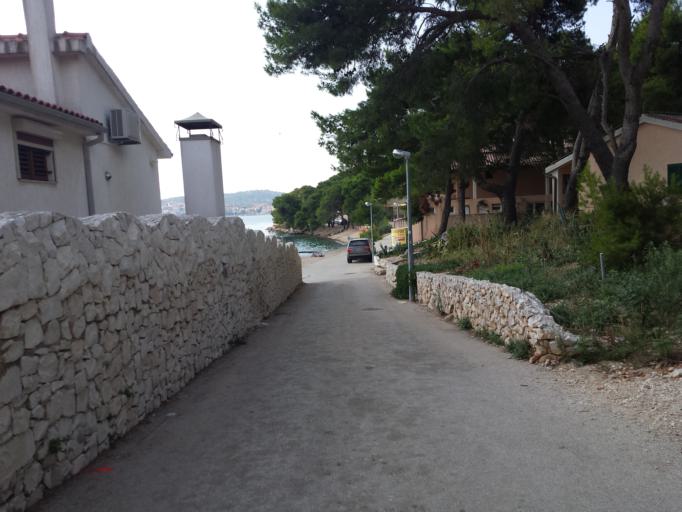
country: HR
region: Sibensko-Kniniska
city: Rogoznica
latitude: 43.5248
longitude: 15.9736
